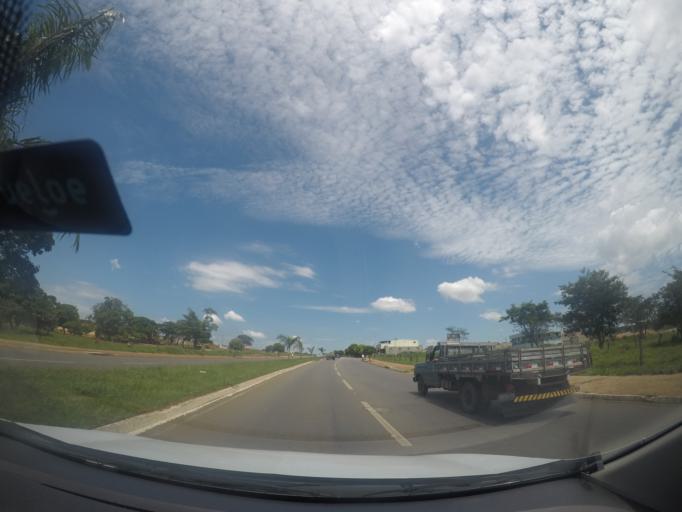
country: BR
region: Goias
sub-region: Goiania
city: Goiania
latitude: -16.6841
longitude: -49.3403
